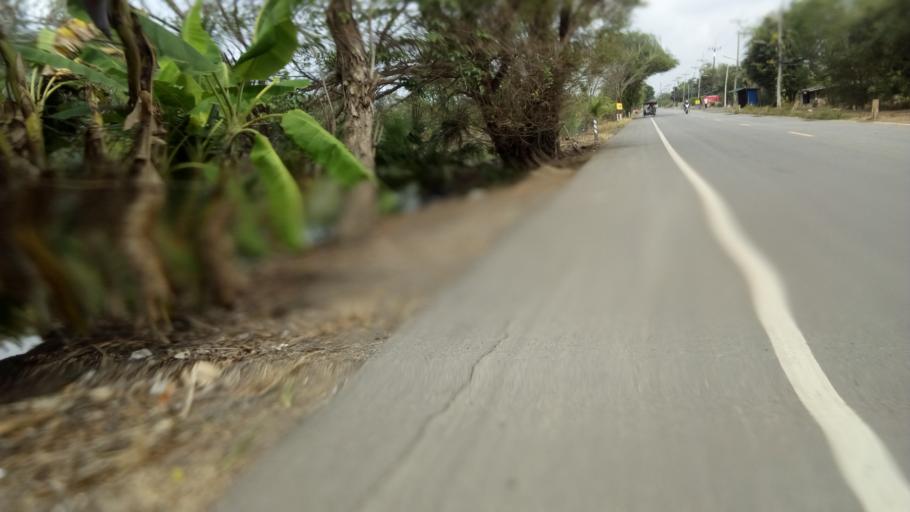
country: TH
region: Pathum Thani
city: Nong Suea
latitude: 14.1838
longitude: 100.8236
